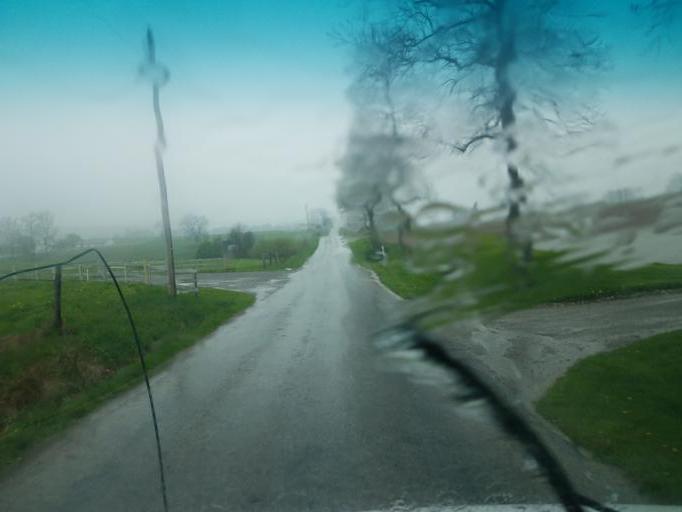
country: US
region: Ohio
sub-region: Stark County
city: Brewster
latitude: 40.6685
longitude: -81.7128
